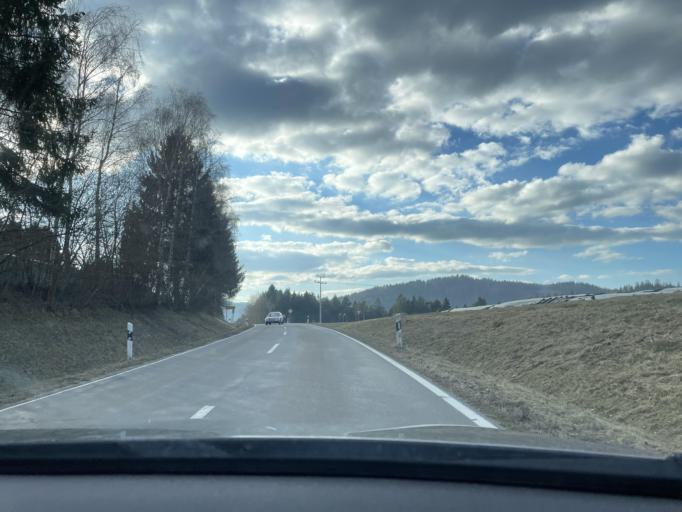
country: DE
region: Bavaria
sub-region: Lower Bavaria
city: Viechtach
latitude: 49.0656
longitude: 12.8715
